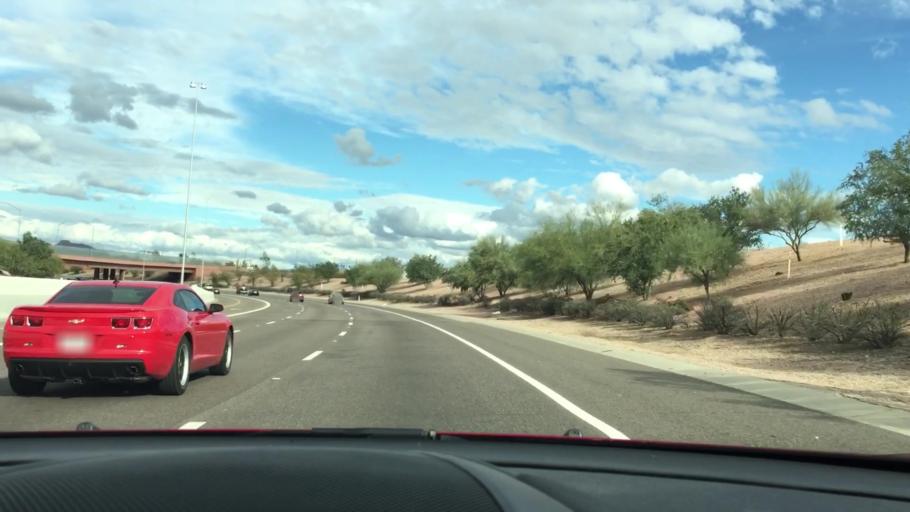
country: US
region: Arizona
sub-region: Maricopa County
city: Mesa
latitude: 33.4673
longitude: -111.7875
